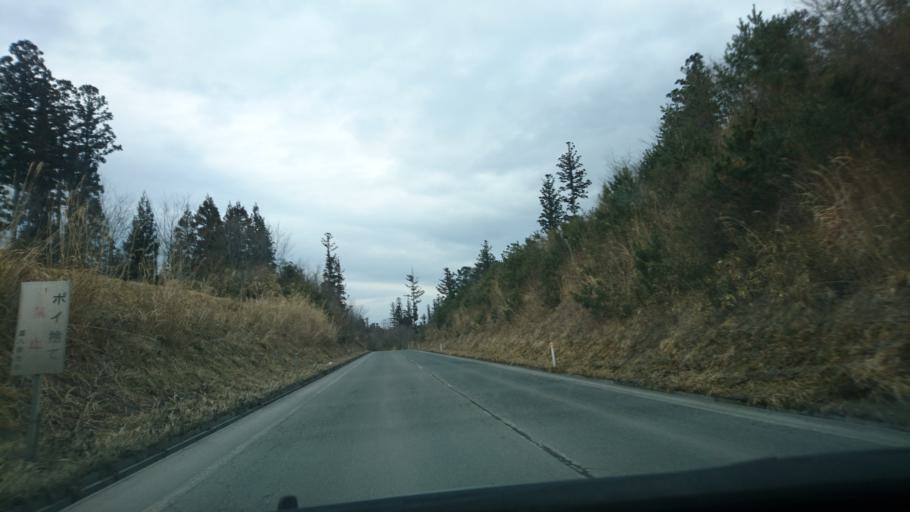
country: JP
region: Iwate
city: Ichinoseki
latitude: 38.9872
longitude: 141.3574
